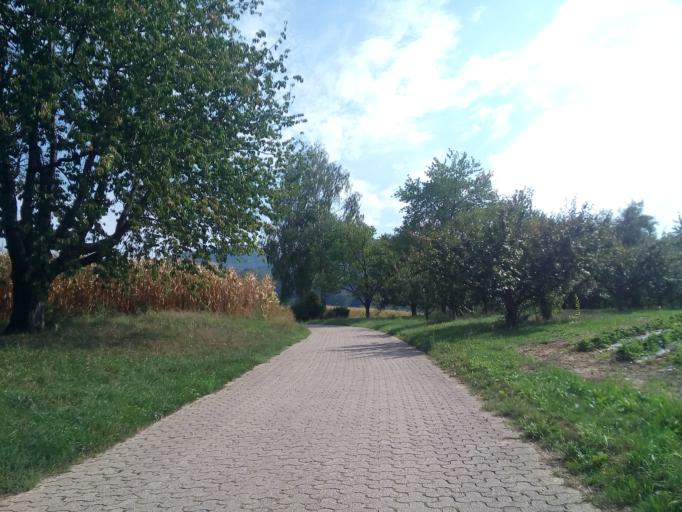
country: DE
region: Baden-Wuerttemberg
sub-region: Freiburg Region
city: Lauf
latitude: 48.6466
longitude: 8.1179
